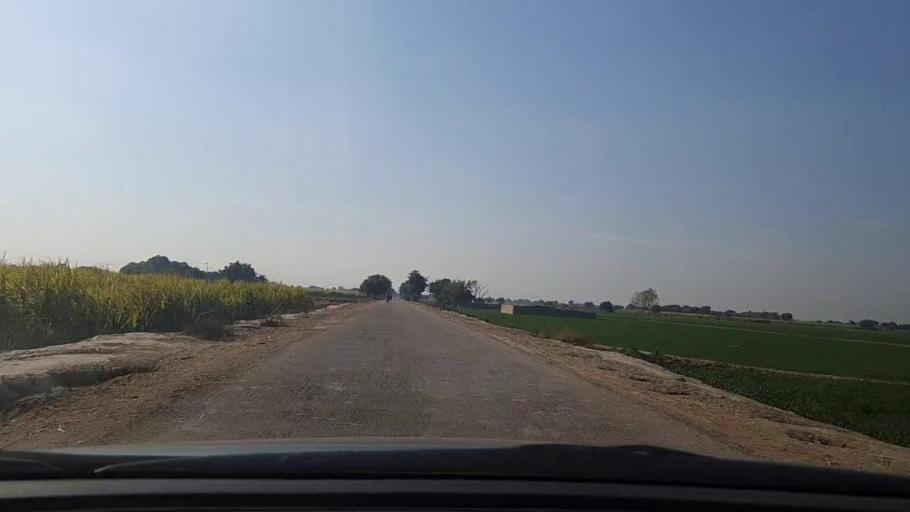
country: PK
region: Sindh
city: Daulatpur
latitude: 26.3205
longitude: 68.0340
